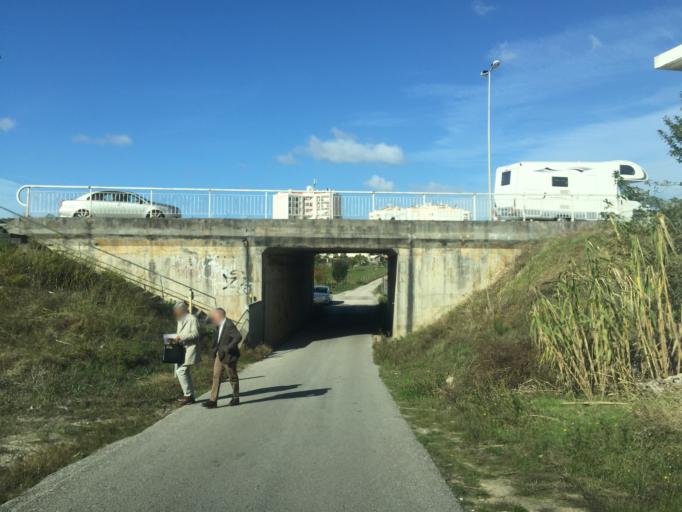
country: PT
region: Coimbra
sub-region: Figueira da Foz
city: Tavarede
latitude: 40.1634
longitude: -8.8434
